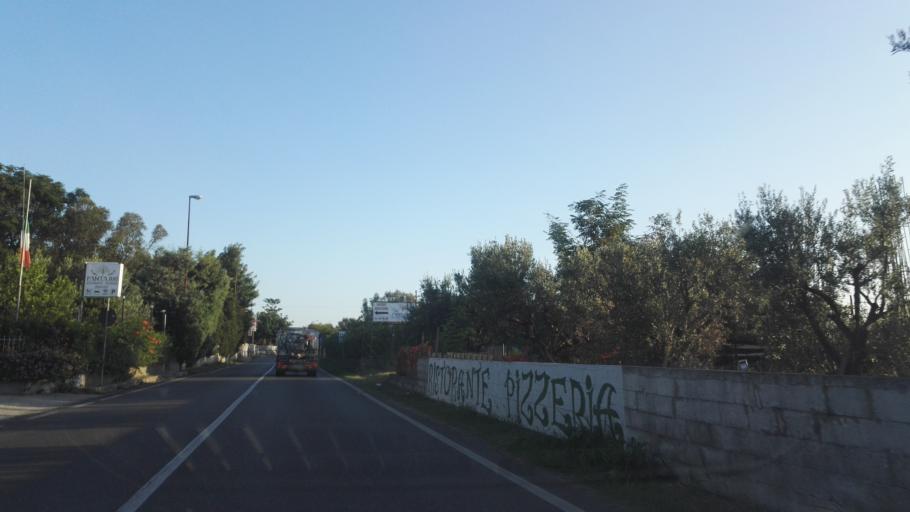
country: IT
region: Calabria
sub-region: Provincia di Catanzaro
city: Badolato Marina
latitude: 38.5830
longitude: 16.5641
